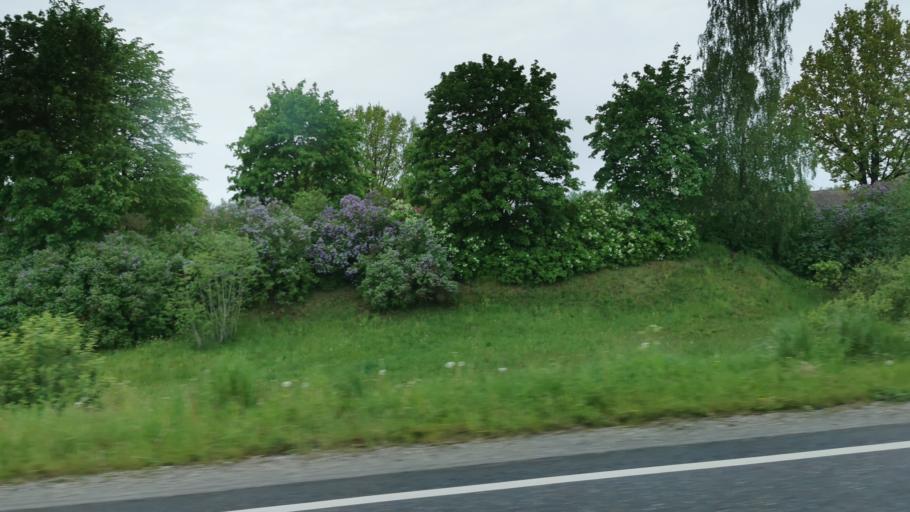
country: EE
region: Laeaene-Virumaa
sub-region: Vaeike-Maarja vald
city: Vaike-Maarja
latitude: 59.1147
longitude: 26.2447
